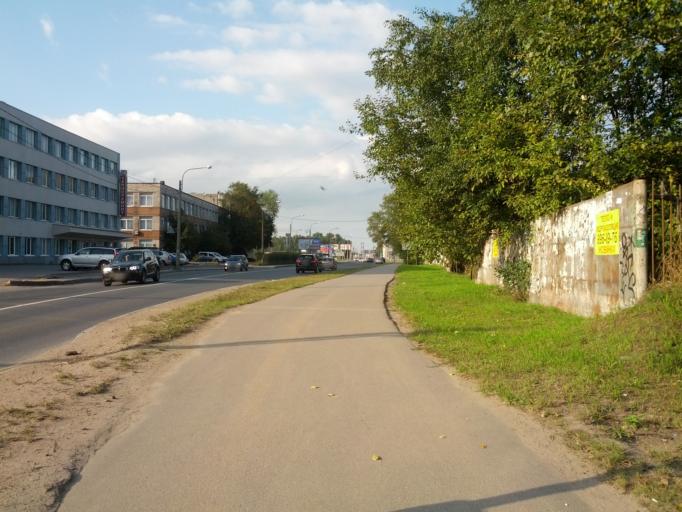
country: RU
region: St.-Petersburg
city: Krasnogvargeisky
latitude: 59.9412
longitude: 30.4351
